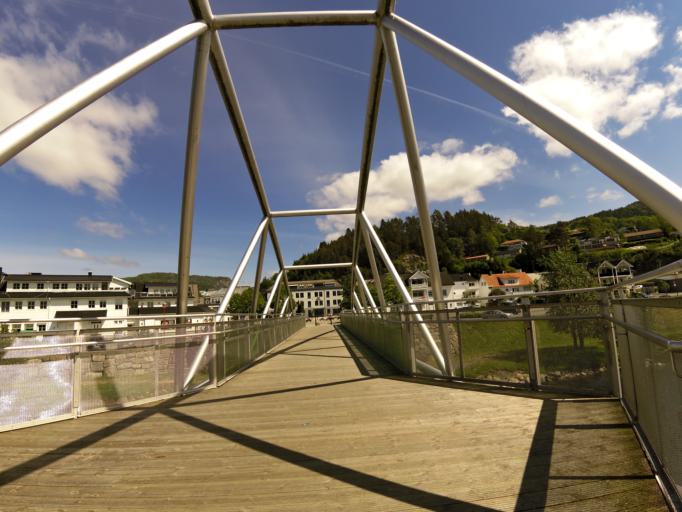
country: NO
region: Vest-Agder
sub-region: Kvinesdal
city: Liknes
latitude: 58.3154
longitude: 6.9610
